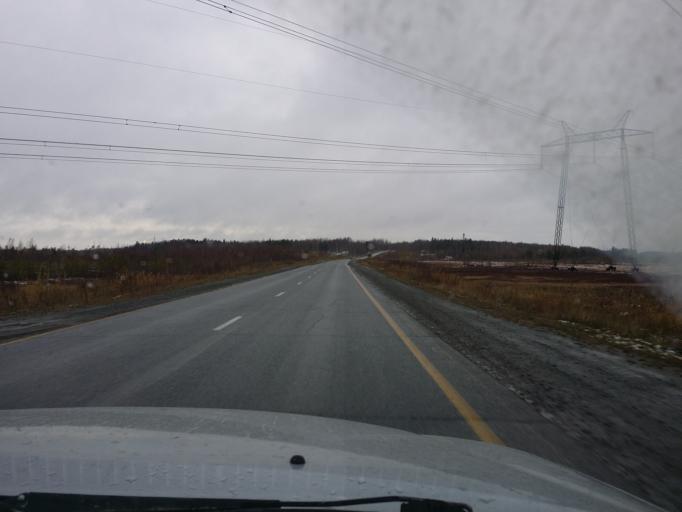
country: RU
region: Khanty-Mansiyskiy Avtonomnyy Okrug
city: Megion
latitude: 61.1071
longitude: 76.0088
